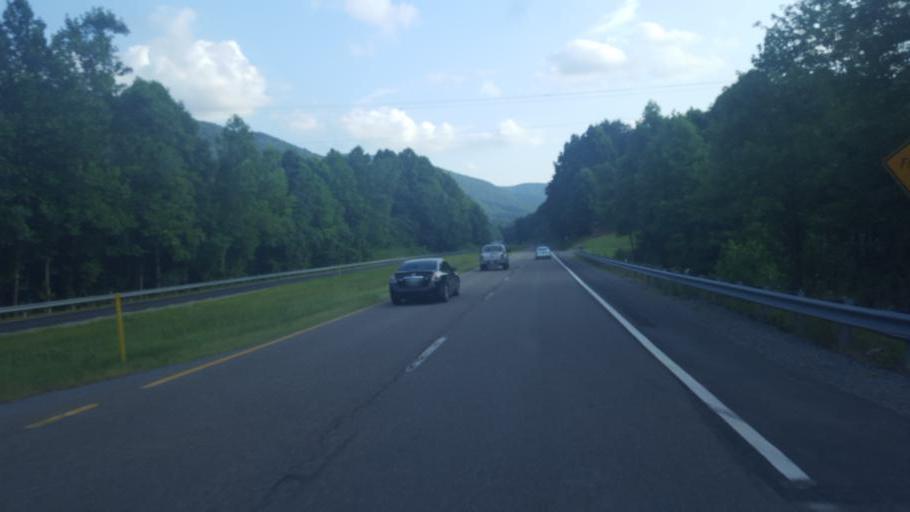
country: US
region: Virginia
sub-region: Wise County
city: Big Stone Gap
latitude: 36.8409
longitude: -82.7639
